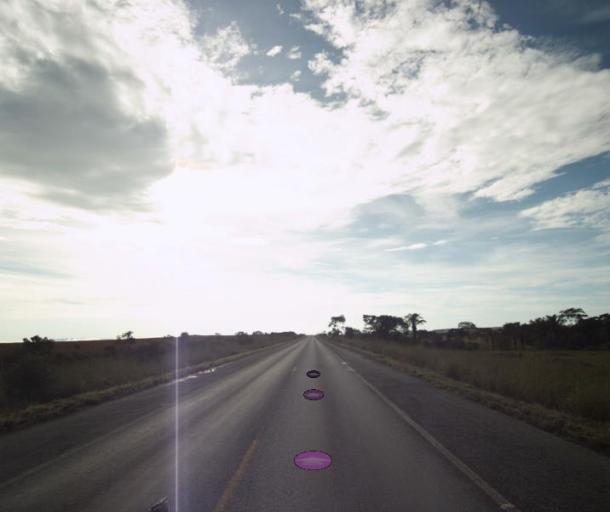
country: BR
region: Goias
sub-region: Pirenopolis
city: Pirenopolis
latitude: -15.7499
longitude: -48.6518
